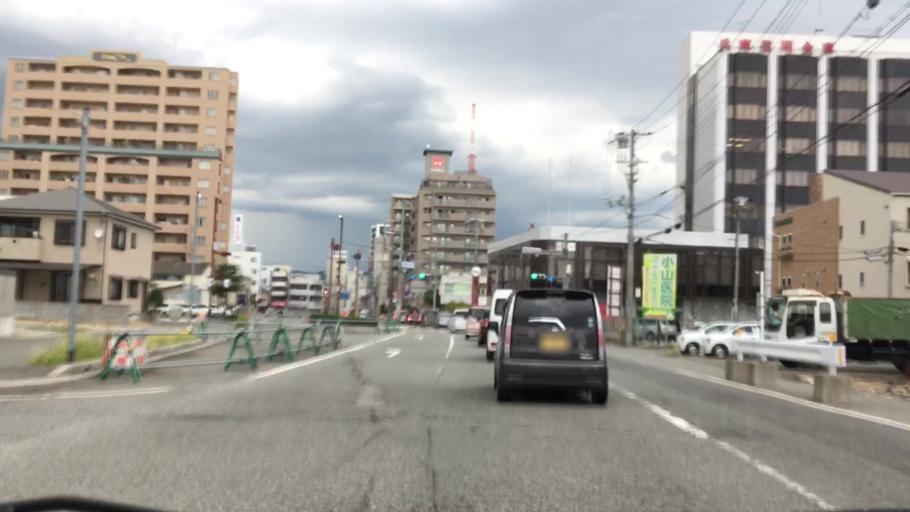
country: JP
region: Hyogo
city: Himeji
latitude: 34.8277
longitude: 134.6960
